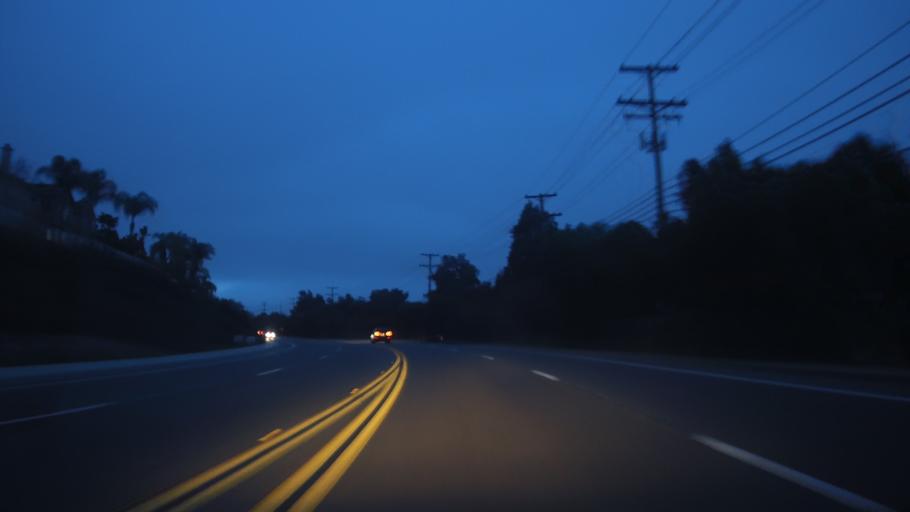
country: US
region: California
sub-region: San Diego County
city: Rancho San Diego
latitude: 32.7428
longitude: -116.9233
